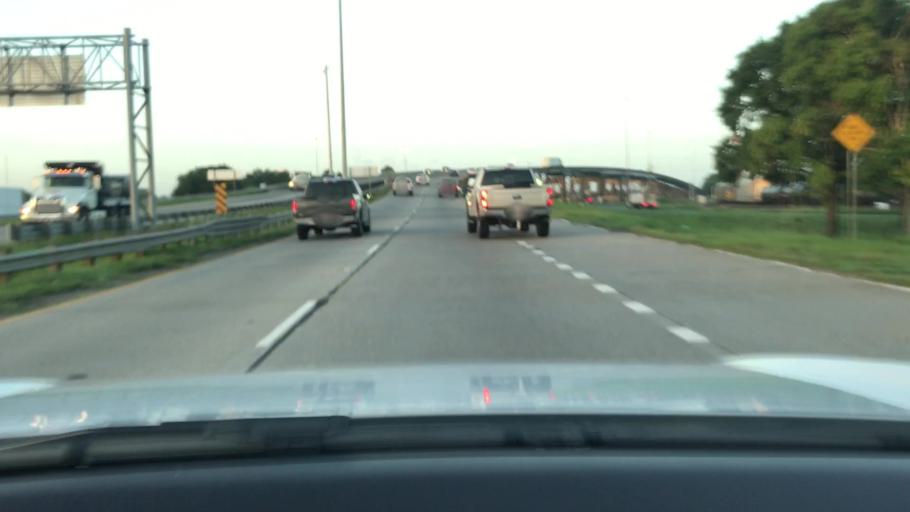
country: US
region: Louisiana
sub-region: West Baton Rouge Parish
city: Port Allen
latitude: 30.4365
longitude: -91.2093
